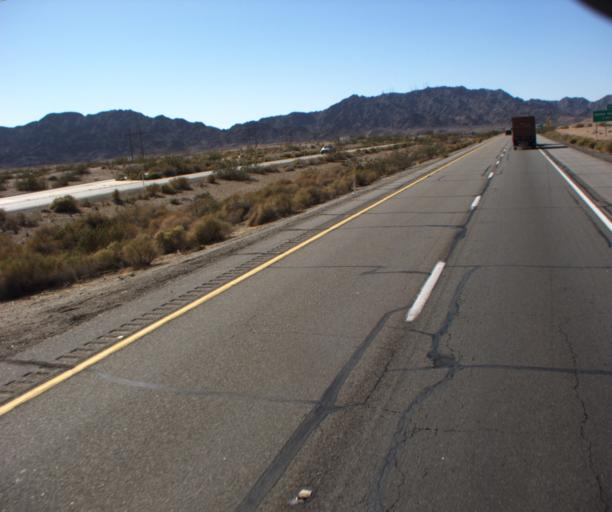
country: US
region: Arizona
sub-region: Yuma County
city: Fortuna Foothills
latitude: 32.6664
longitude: -114.2805
